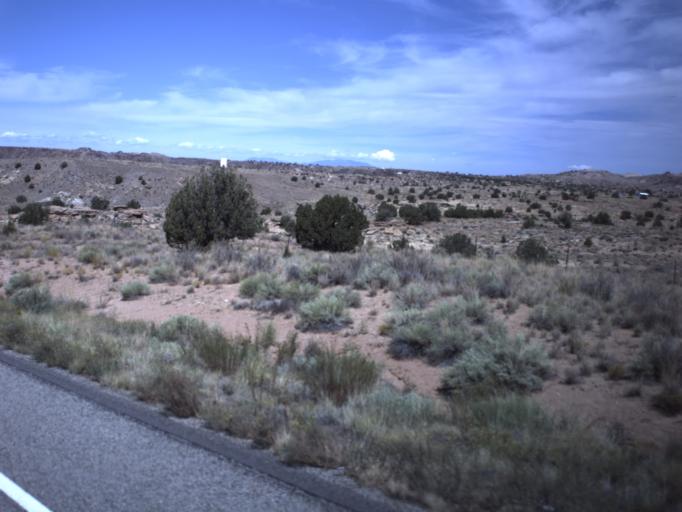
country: US
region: Colorado
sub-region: Montezuma County
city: Towaoc
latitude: 37.1920
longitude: -109.1379
